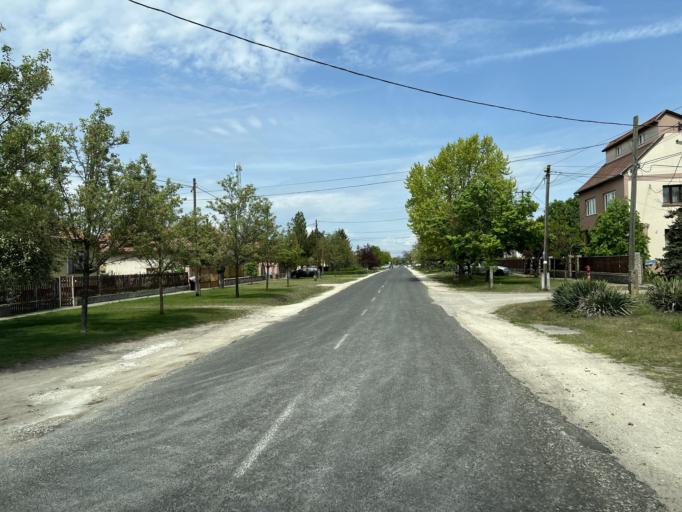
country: HU
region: Pest
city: Csemo
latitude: 47.1138
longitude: 19.6944
